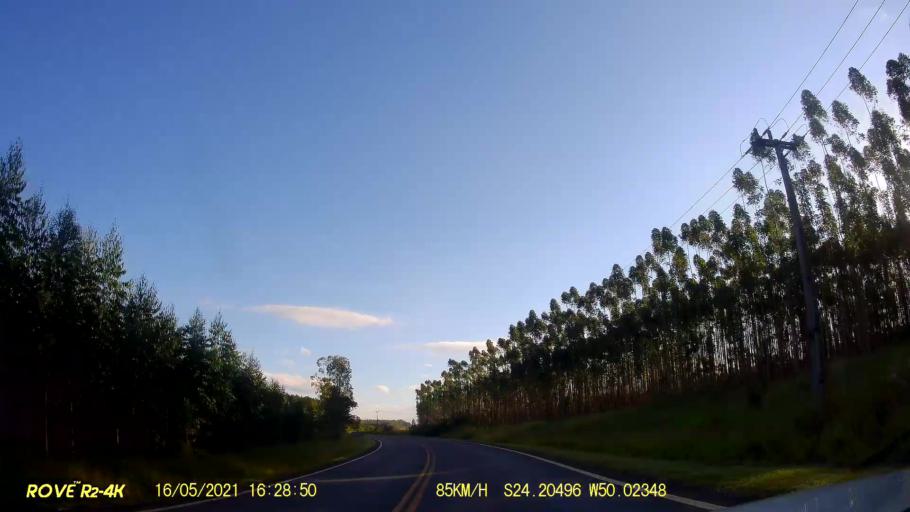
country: BR
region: Parana
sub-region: Jaguariaiva
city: Jaguariaiva
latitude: -24.2050
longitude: -50.0238
